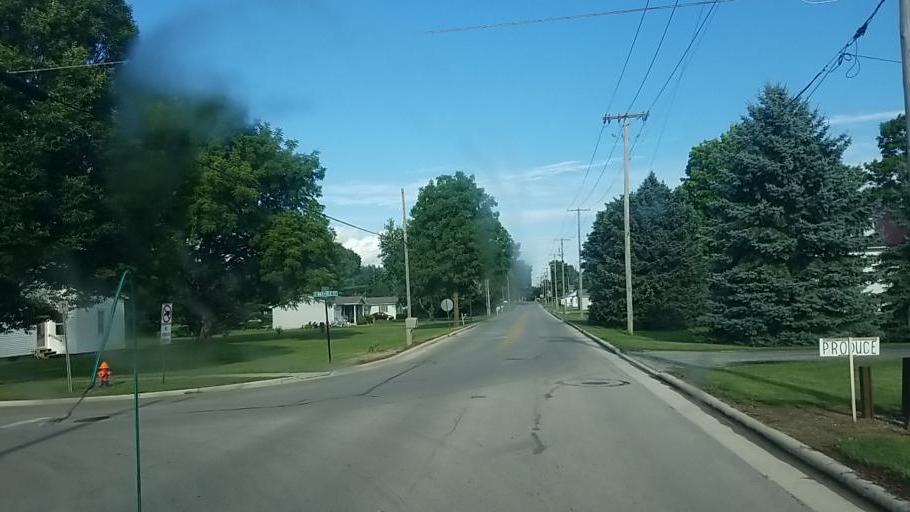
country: US
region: Ohio
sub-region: Wyandot County
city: Upper Sandusky
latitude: 40.8180
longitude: -83.2904
